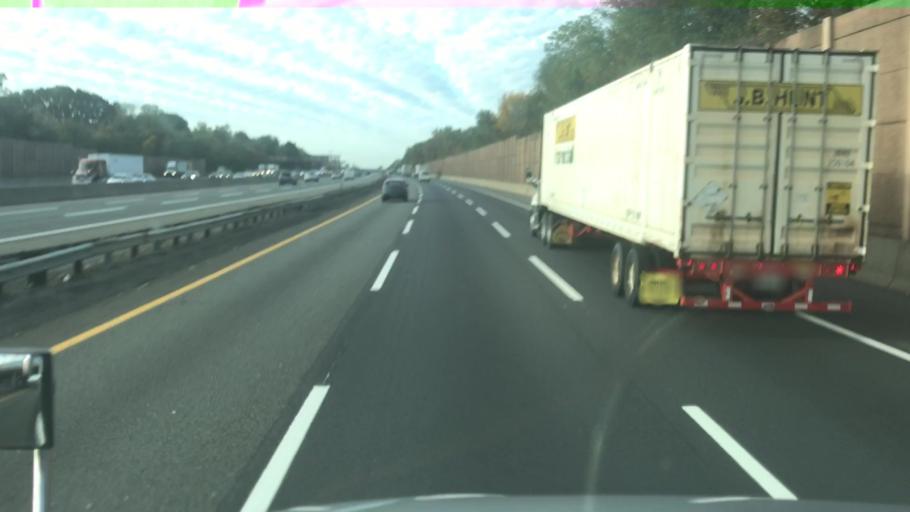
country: US
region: New Jersey
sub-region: Middlesex County
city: Metuchen
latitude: 40.5142
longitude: -74.3677
